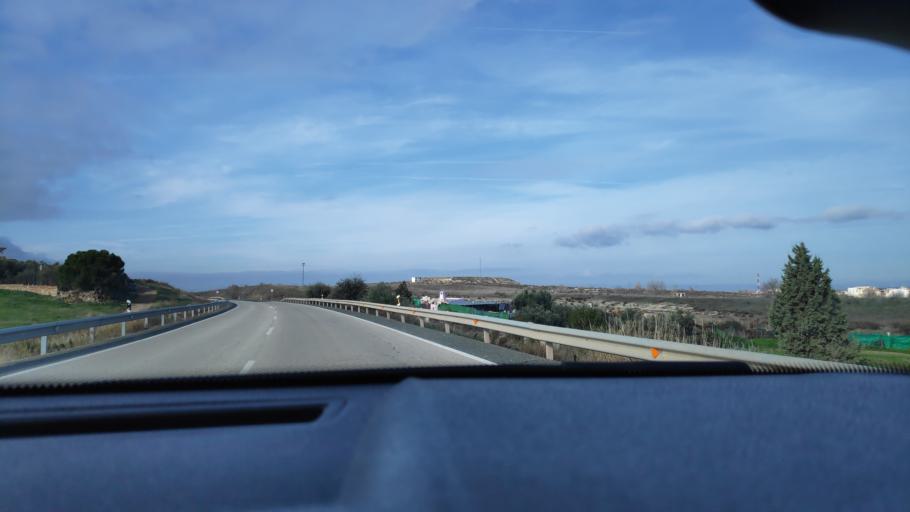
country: ES
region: Andalusia
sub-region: Provincia de Jaen
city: Linares
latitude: 38.0828
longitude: -3.6256
